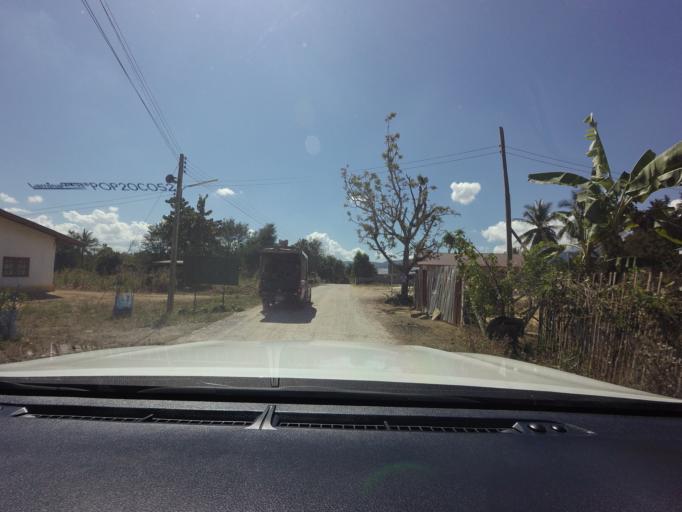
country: TH
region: Nakhon Ratchasima
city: Wang Nam Khiao
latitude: 14.4657
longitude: 101.6605
